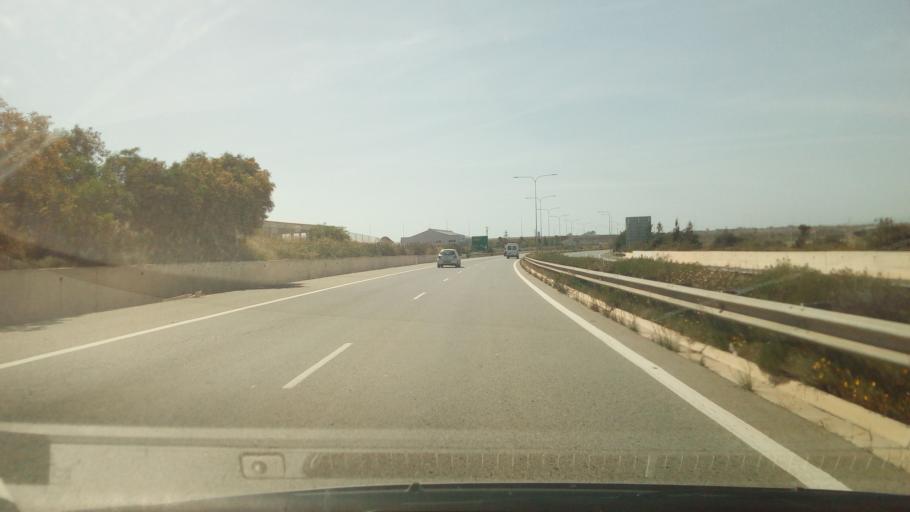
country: CY
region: Ammochostos
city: Liopetri
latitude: 34.9690
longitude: 33.8683
